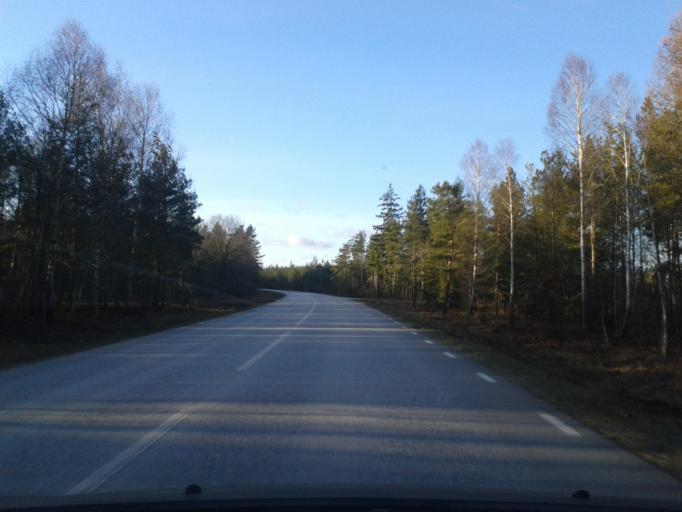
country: SE
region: Gotland
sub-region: Gotland
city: Slite
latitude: 57.4361
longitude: 18.6638
